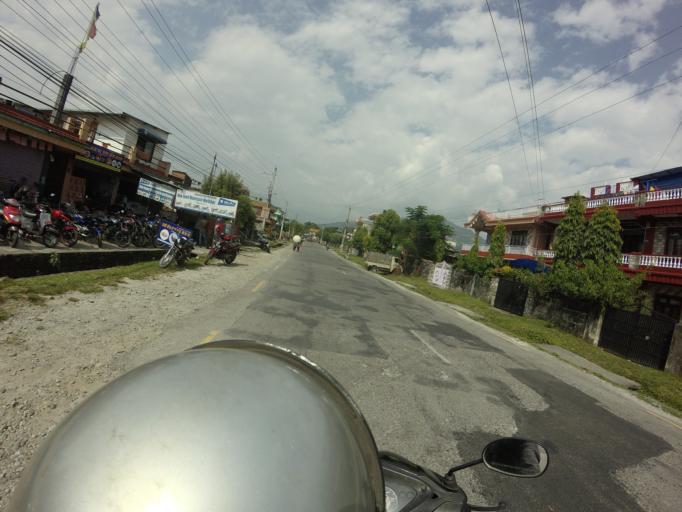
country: NP
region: Western Region
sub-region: Gandaki Zone
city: Pokhara
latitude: 28.2091
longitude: 84.0005
